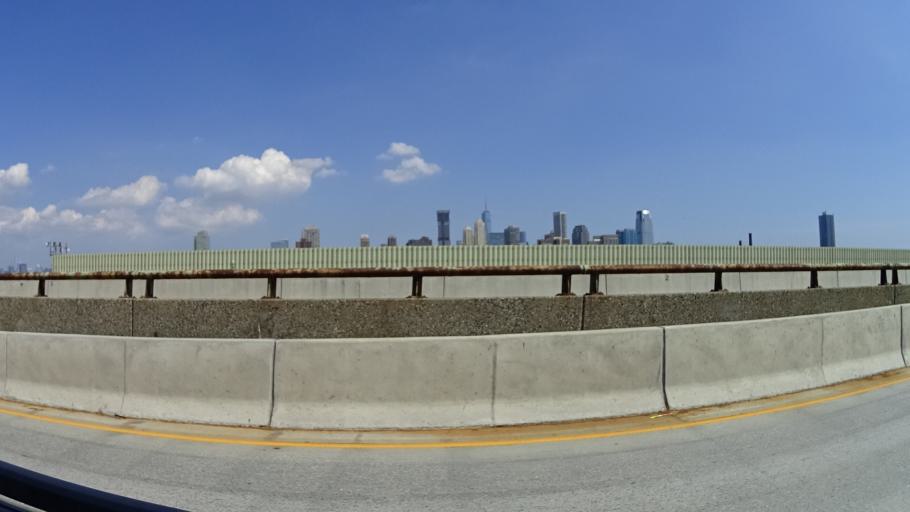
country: US
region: New Jersey
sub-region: Hudson County
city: Jersey City
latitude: 40.7246
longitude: -74.0539
